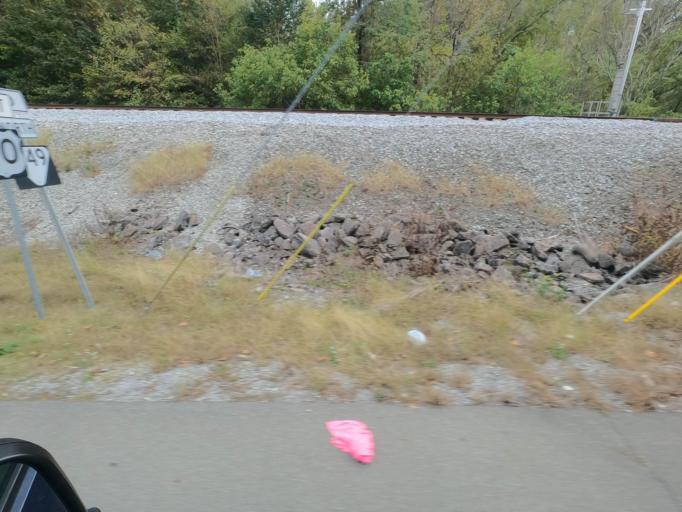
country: US
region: Tennessee
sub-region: Cheatham County
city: Pegram
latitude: 36.1081
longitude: -87.0710
